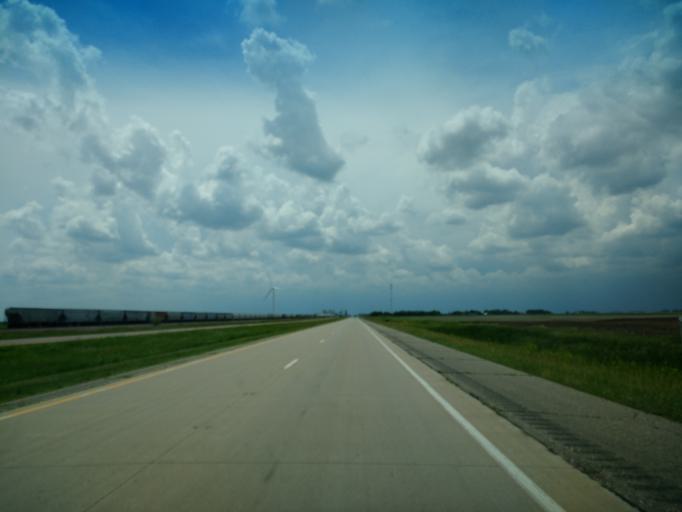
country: US
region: Minnesota
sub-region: Nobles County
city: Worthington
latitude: 43.7283
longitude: -95.4262
